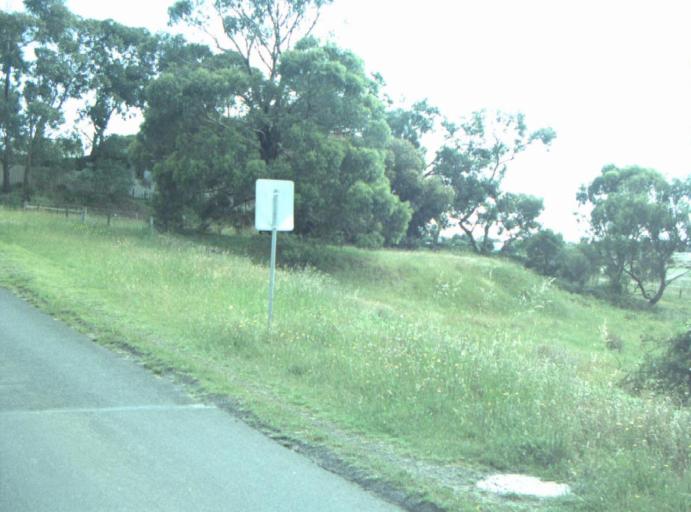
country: AU
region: Victoria
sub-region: Greater Geelong
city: Clifton Springs
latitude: -38.1781
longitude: 144.5698
